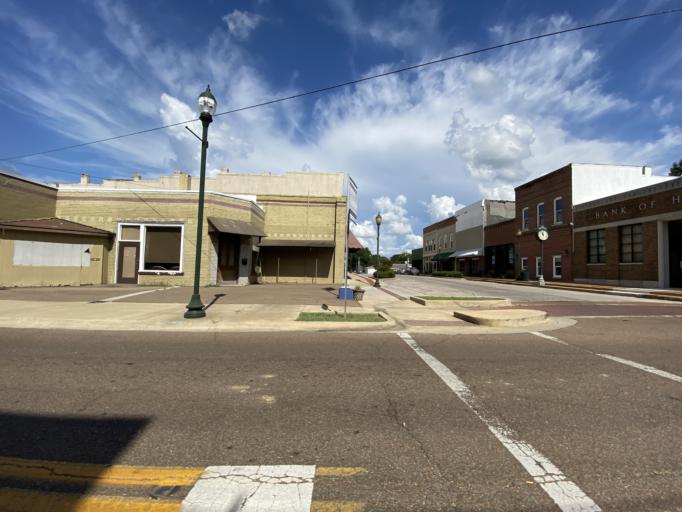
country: US
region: Tennessee
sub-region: Lauderdale County
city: Halls
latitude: 35.8755
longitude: -89.3960
